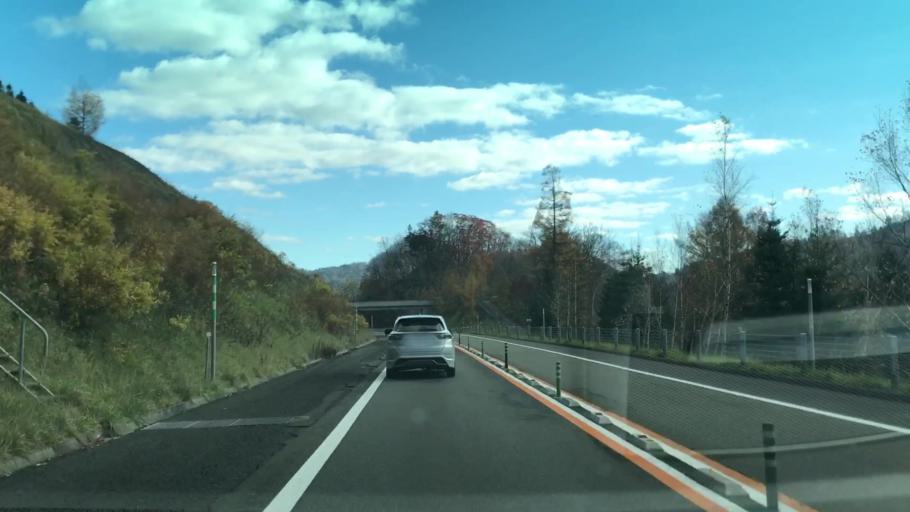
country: JP
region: Hokkaido
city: Chitose
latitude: 42.9107
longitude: 141.9797
